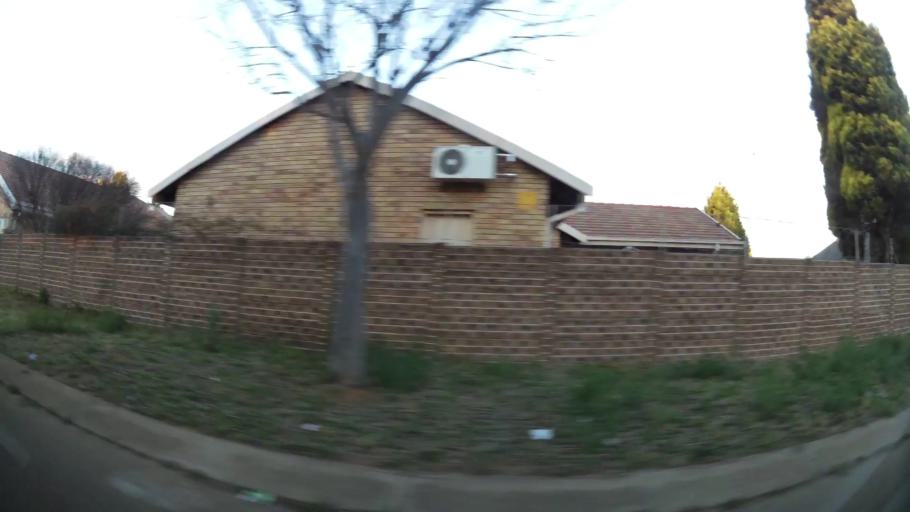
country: ZA
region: North-West
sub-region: Dr Kenneth Kaunda District Municipality
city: Potchefstroom
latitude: -26.7242
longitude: 27.1146
